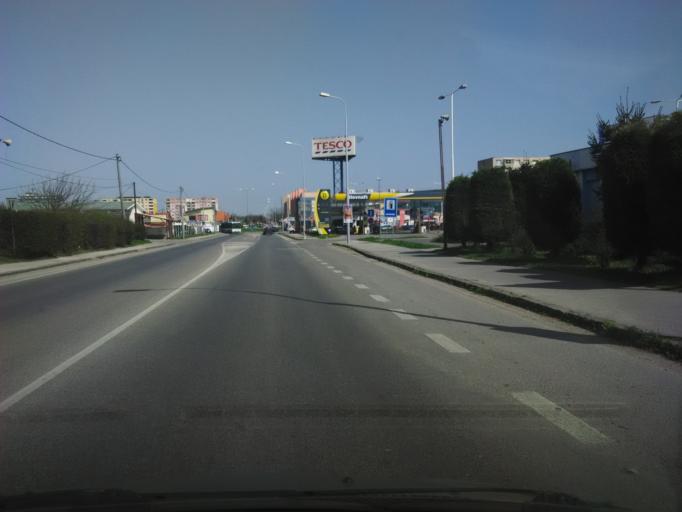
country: SK
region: Nitriansky
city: Sellye
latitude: 48.1632
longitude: 17.8835
